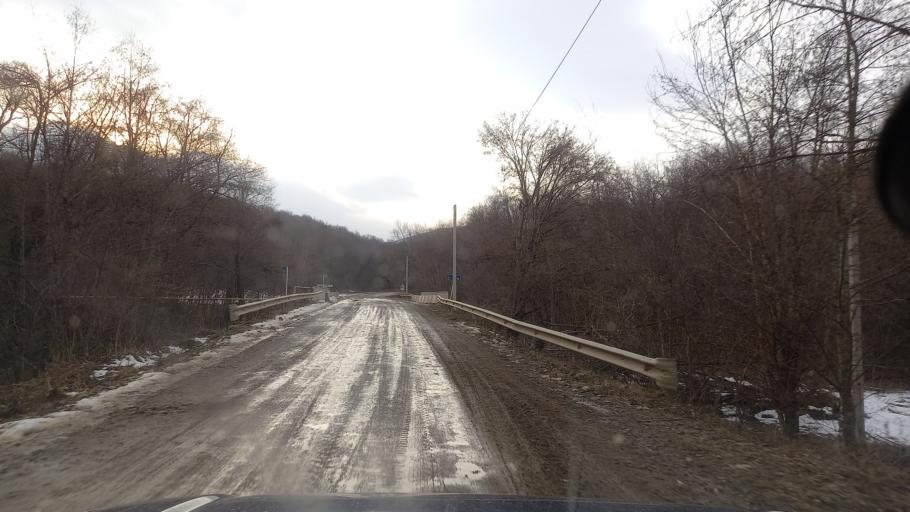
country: RU
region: Adygeya
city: Kamennomostskiy
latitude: 44.1424
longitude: 40.2766
